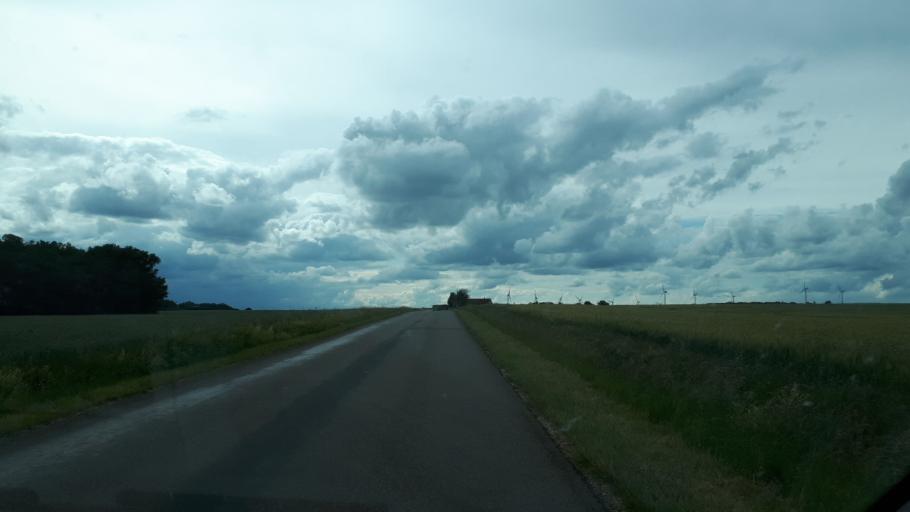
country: FR
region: Centre
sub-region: Departement du Cher
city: Massay
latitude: 47.0976
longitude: 1.9814
